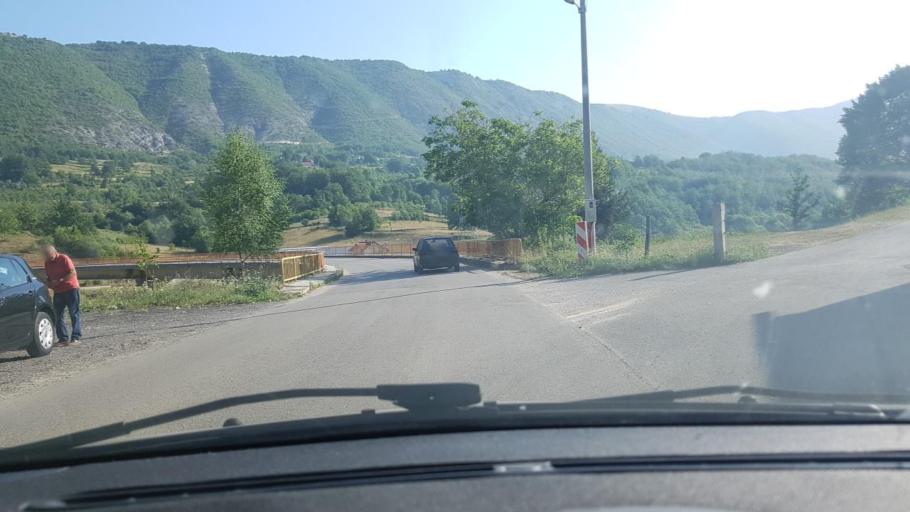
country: BA
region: Federation of Bosnia and Herzegovina
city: Rumboci
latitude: 43.8275
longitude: 17.5221
